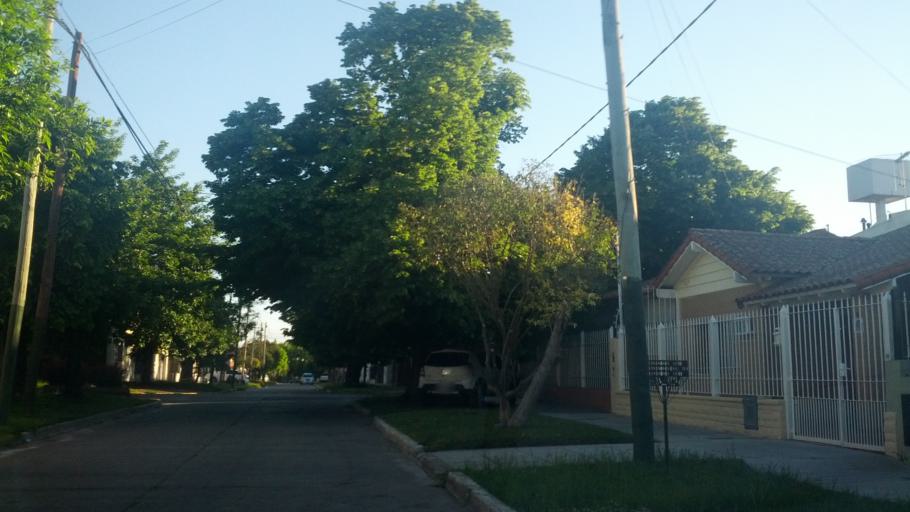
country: AR
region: Buenos Aires
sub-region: Partido de Lomas de Zamora
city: Lomas de Zamora
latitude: -34.7680
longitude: -58.4147
